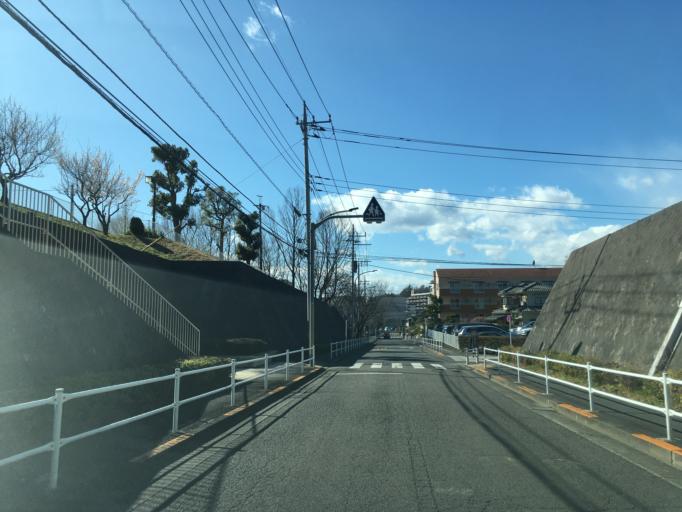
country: JP
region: Tokyo
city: Hino
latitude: 35.6143
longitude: 139.4148
